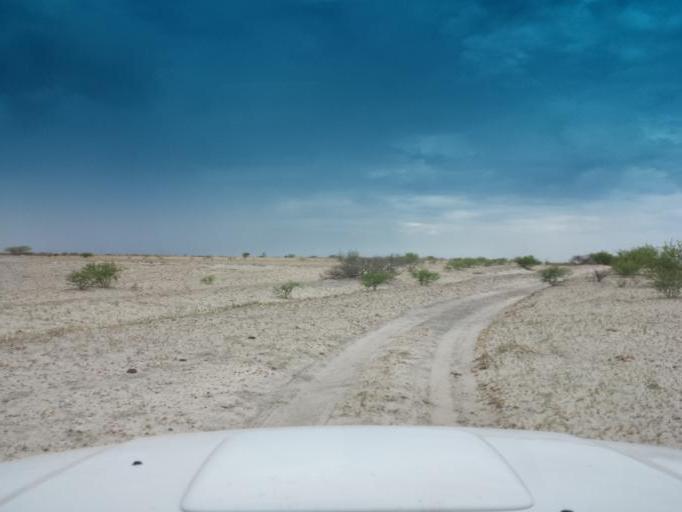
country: BW
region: Central
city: Mopipi
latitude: -21.1797
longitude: 24.8682
